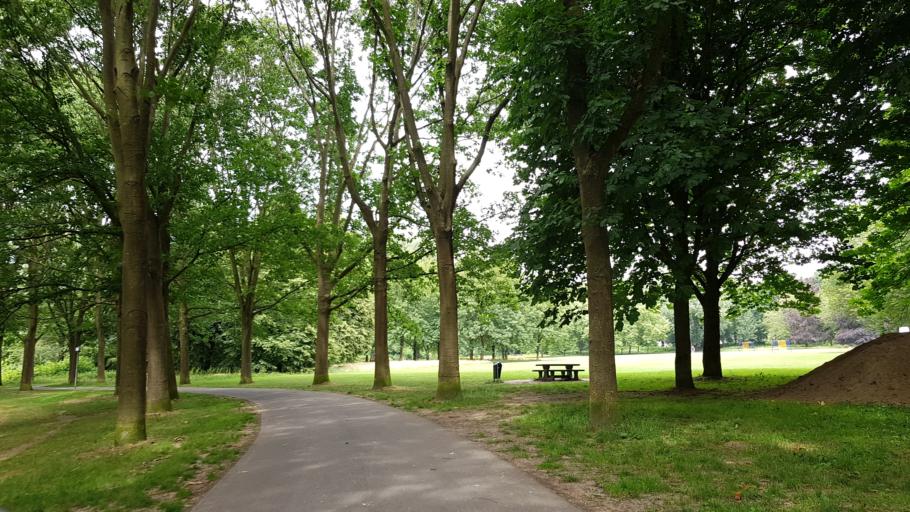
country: NL
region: Gelderland
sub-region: Gemeente Apeldoorn
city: Apeldoorn
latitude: 52.1958
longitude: 5.9986
